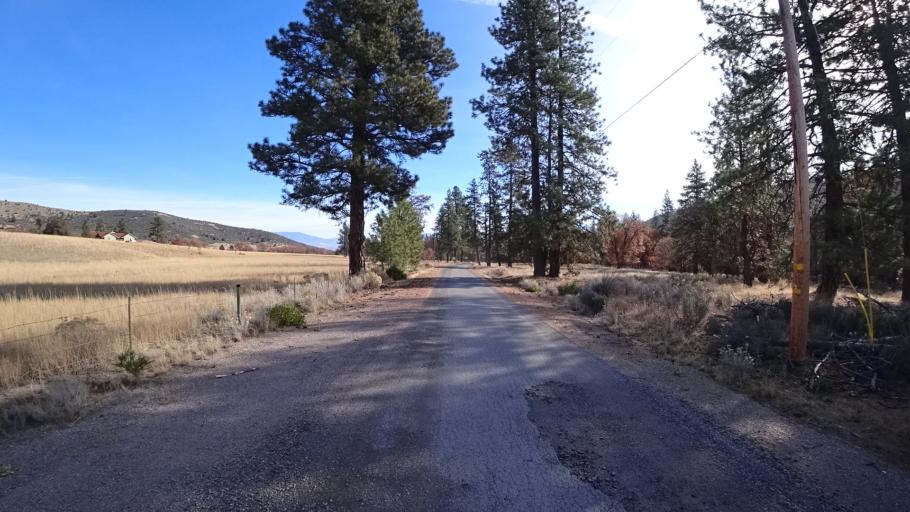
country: US
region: California
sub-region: Siskiyou County
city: Yreka
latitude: 41.5416
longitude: -122.5954
